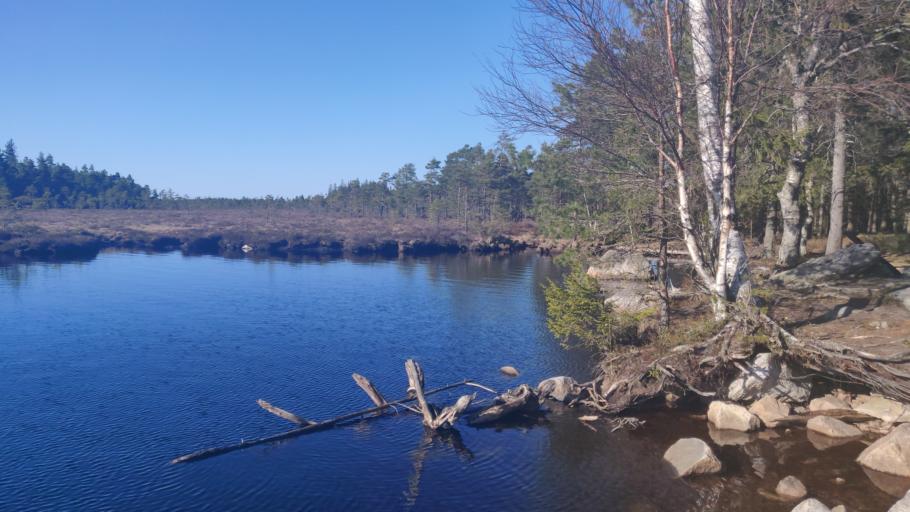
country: SE
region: Joenkoeping
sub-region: Mullsjo Kommun
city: Mullsjoe
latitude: 57.7057
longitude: 13.6929
